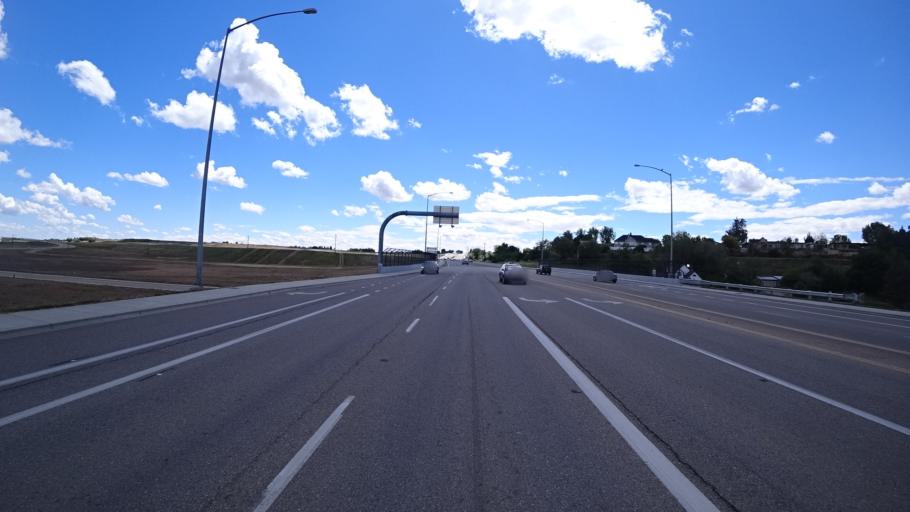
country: US
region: Idaho
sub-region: Ada County
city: Meridian
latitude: 43.5923
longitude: -116.4340
